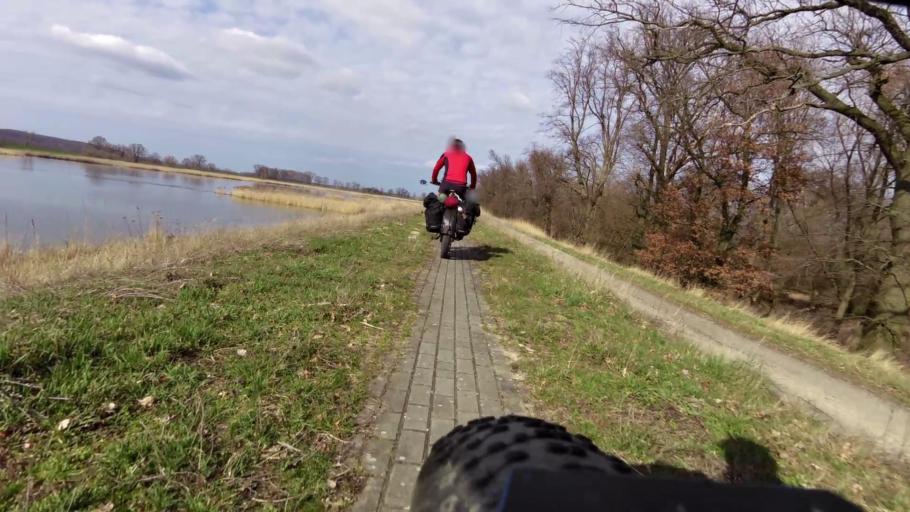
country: DE
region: Brandenburg
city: Reitwein
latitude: 52.4702
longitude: 14.6137
